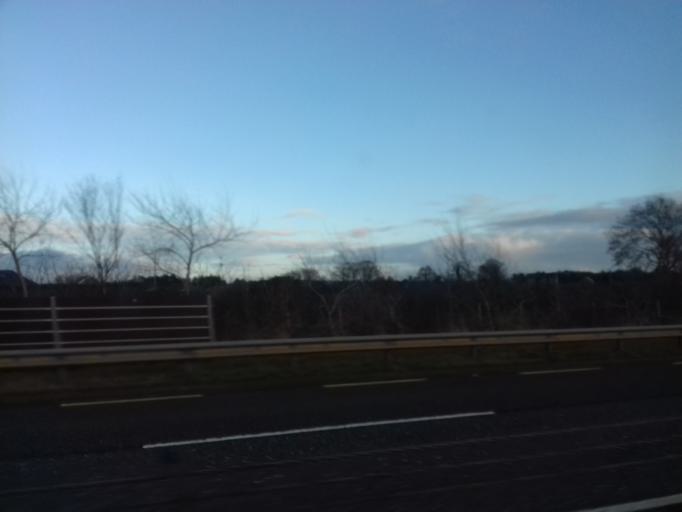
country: IE
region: Ulster
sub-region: County Monaghan
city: Castleblayney
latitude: 54.1571
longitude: -6.8021
